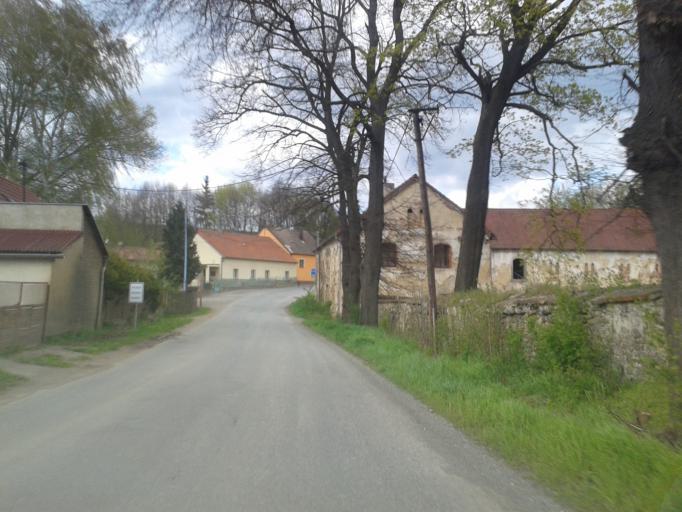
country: CZ
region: Central Bohemia
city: Revnice
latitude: 49.9107
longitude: 14.1525
